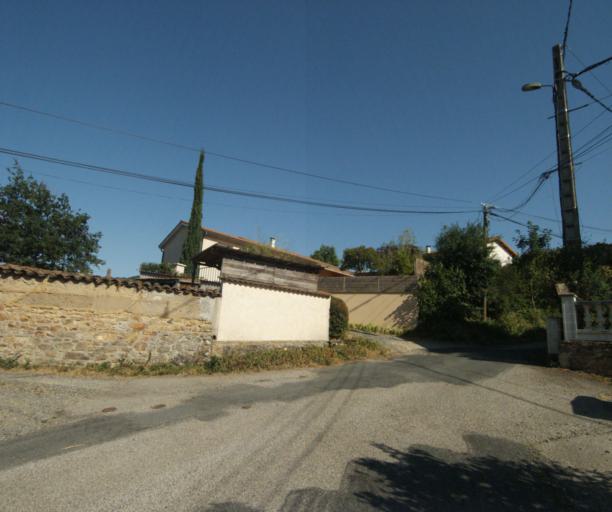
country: FR
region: Rhone-Alpes
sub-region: Departement du Rhone
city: Saint-Pierre-la-Palud
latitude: 45.7748
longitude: 4.6074
